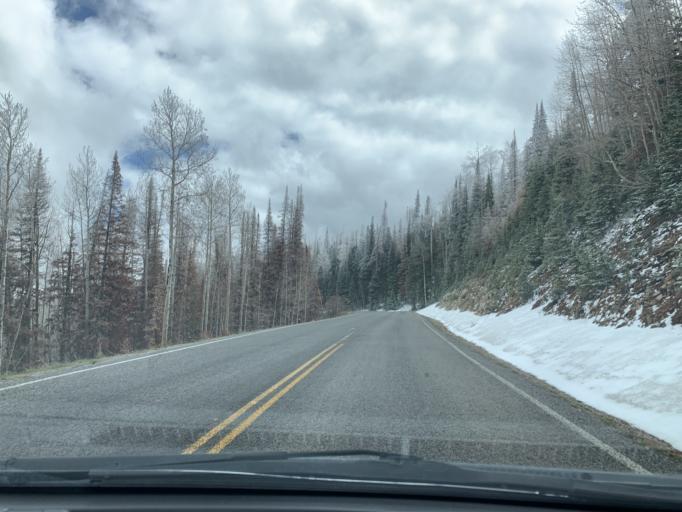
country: US
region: Utah
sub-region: Utah County
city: Santaquin
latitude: 39.8636
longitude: -111.6891
